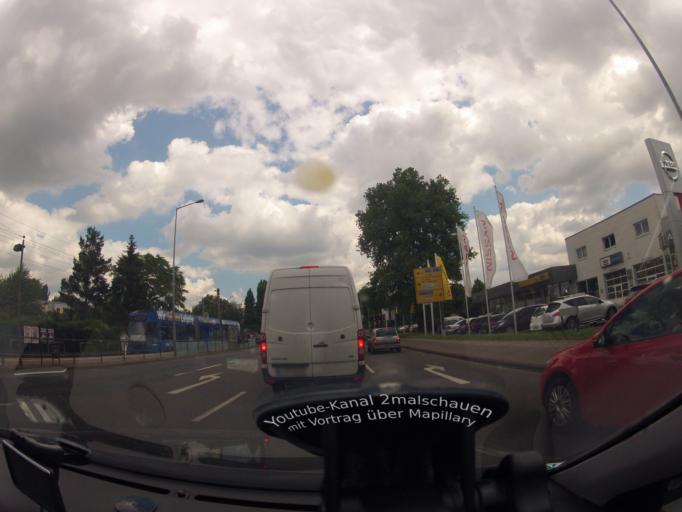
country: DE
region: Saxony
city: Leipzig
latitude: 51.3513
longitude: 12.4254
